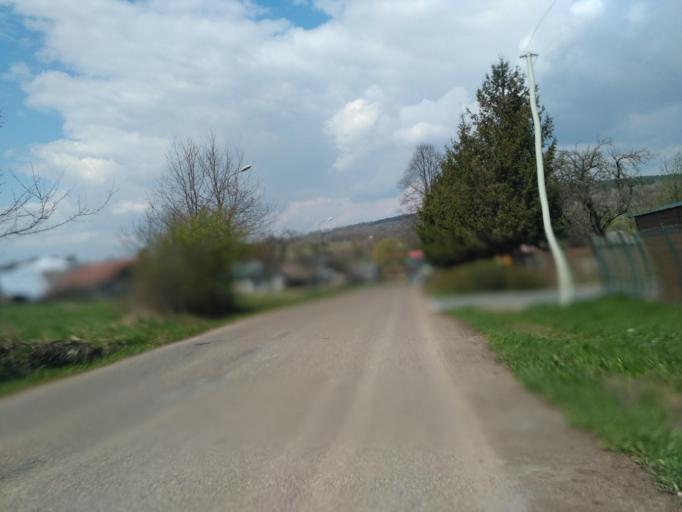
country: PL
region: Subcarpathian Voivodeship
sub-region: Powiat sanocki
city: Nowosielce-Gniewosz
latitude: 49.5559
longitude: 22.1055
